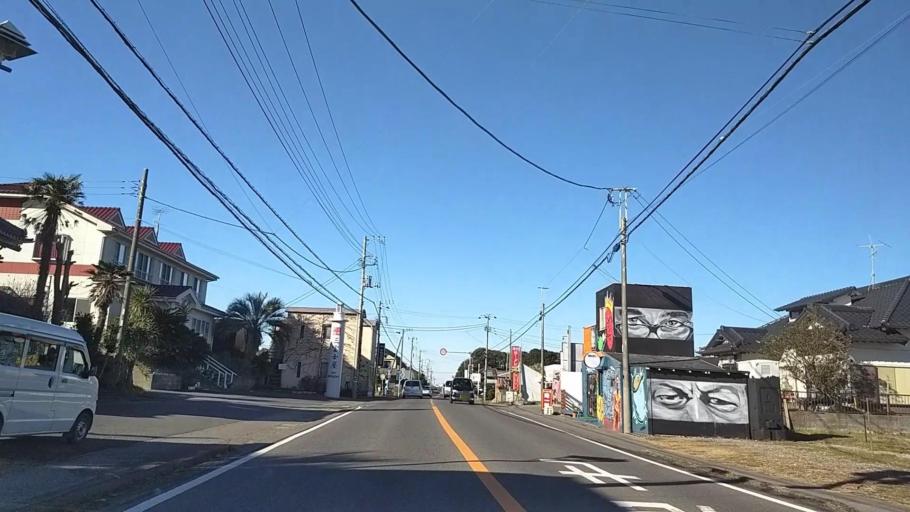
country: JP
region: Chiba
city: Ohara
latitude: 35.3272
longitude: 140.3983
